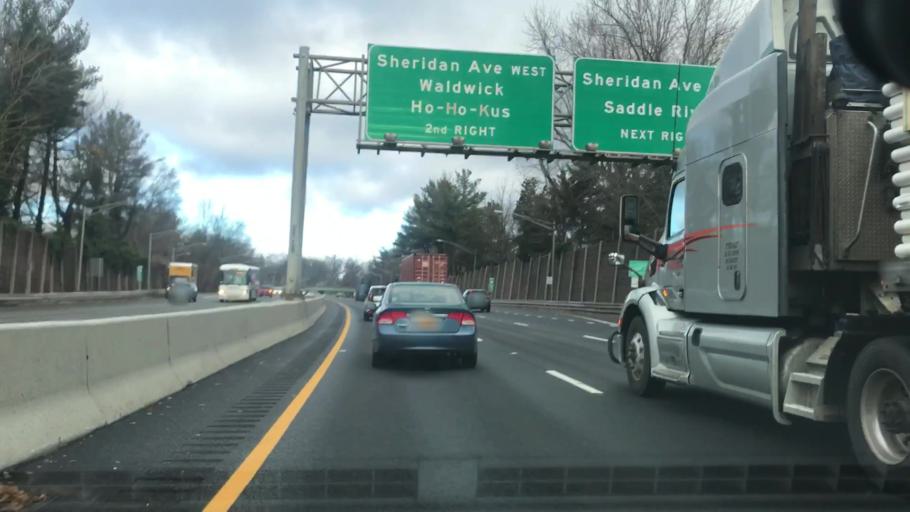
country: US
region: New Jersey
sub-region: Bergen County
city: Ho-Ho-Kus
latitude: 41.0076
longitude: -74.1038
